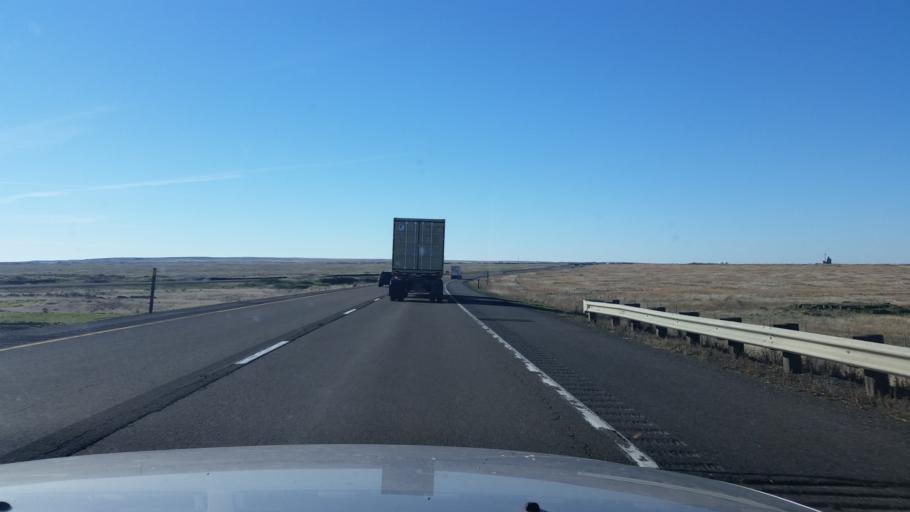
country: US
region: Washington
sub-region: Adams County
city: Ritzville
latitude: 47.2463
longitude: -118.1134
